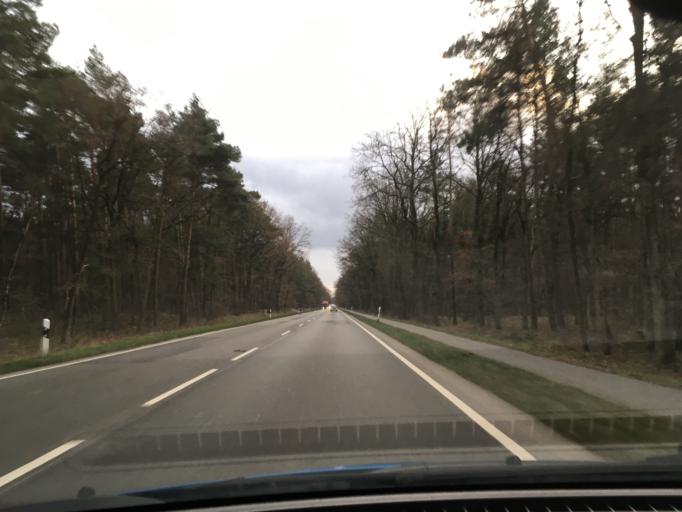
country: DE
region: Lower Saxony
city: Brietlingen
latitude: 53.3114
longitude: 10.4310
